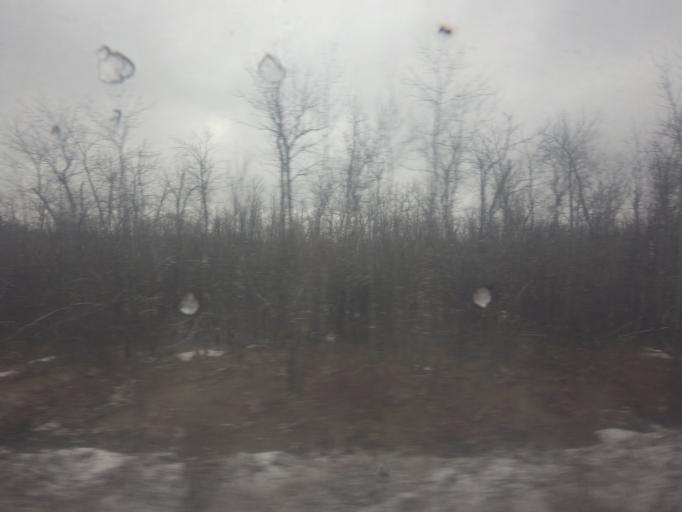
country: CA
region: Ontario
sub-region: Lanark County
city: Smiths Falls
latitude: 44.9430
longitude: -76.0195
